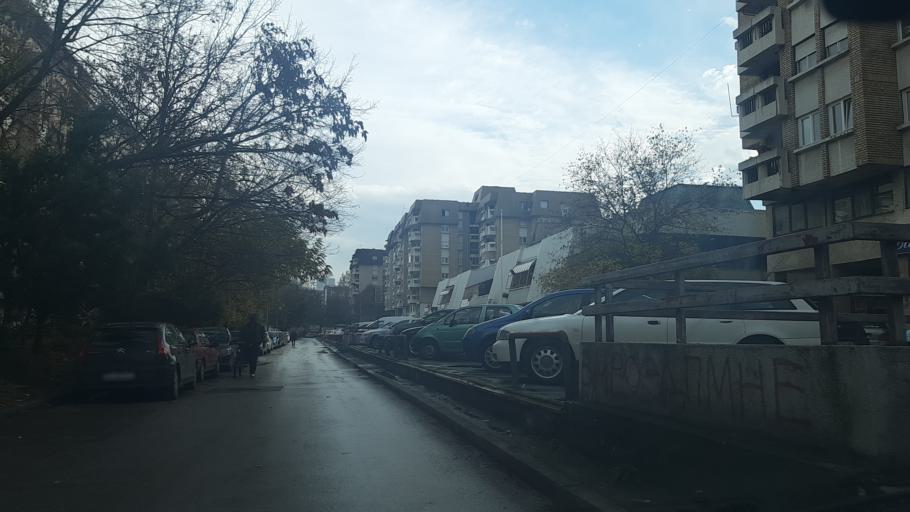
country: MK
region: Karpos
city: Skopje
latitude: 41.9899
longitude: 21.4502
